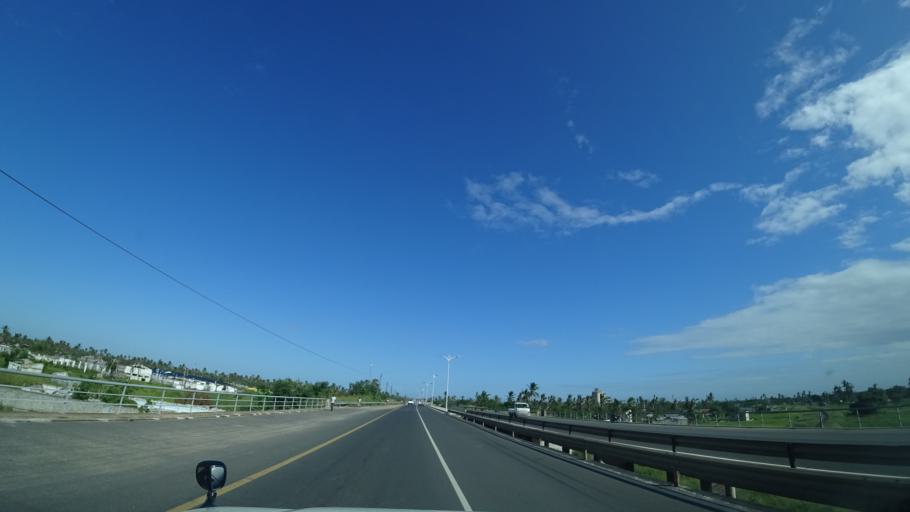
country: MZ
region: Sofala
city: Beira
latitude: -19.7393
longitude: 34.8533
